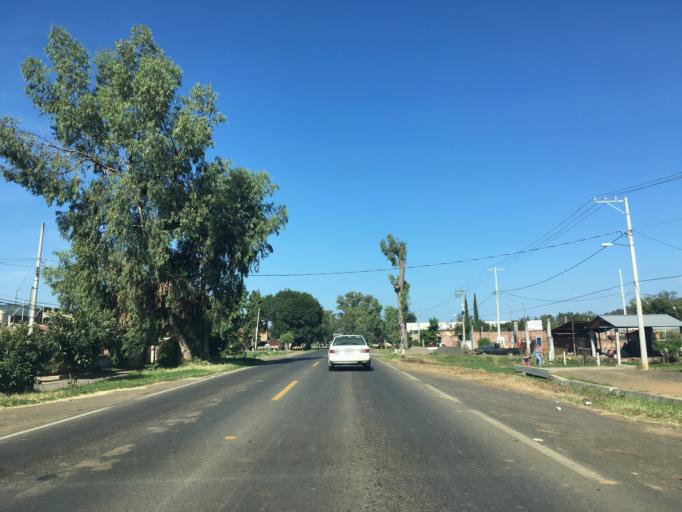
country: MX
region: Mexico
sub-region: Chalco
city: Chilchota
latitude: 19.8470
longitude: -102.1053
